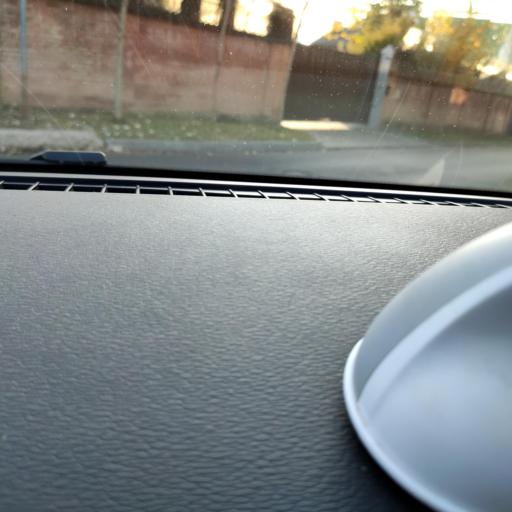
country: RU
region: Samara
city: Samara
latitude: 53.2270
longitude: 50.1669
